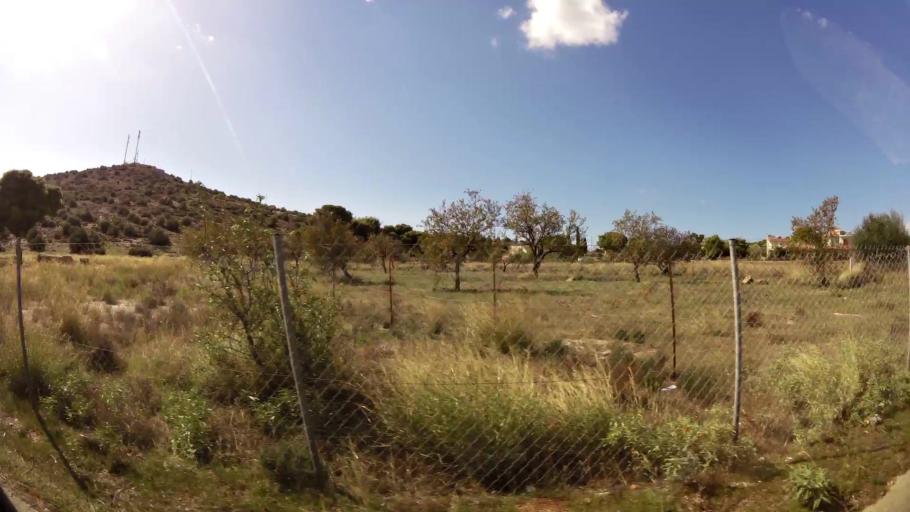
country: GR
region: Attica
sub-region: Nomarchia Anatolikis Attikis
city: Vari
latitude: 37.8404
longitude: 23.8007
